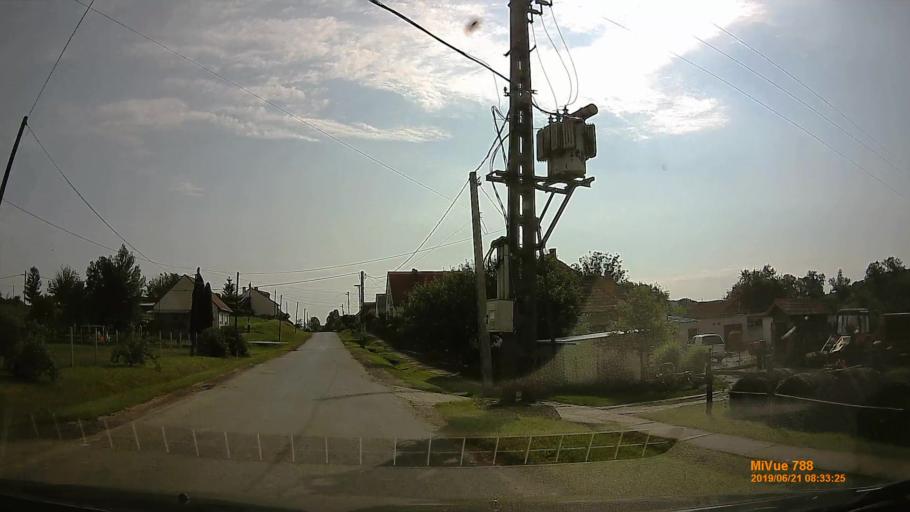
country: HU
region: Baranya
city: Buekkoesd
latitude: 46.1619
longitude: 17.8799
